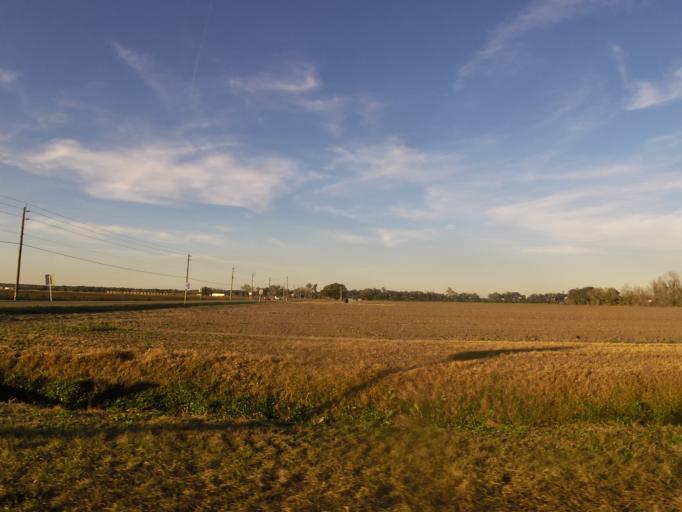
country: US
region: Florida
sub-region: Saint Johns County
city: Saint Augustine Shores
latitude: 29.7910
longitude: -81.4838
